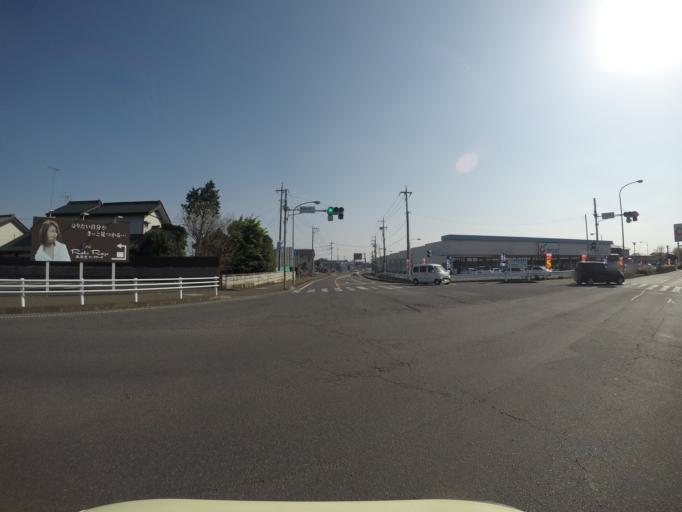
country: JP
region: Ibaraki
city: Yuki
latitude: 36.2867
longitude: 139.8810
